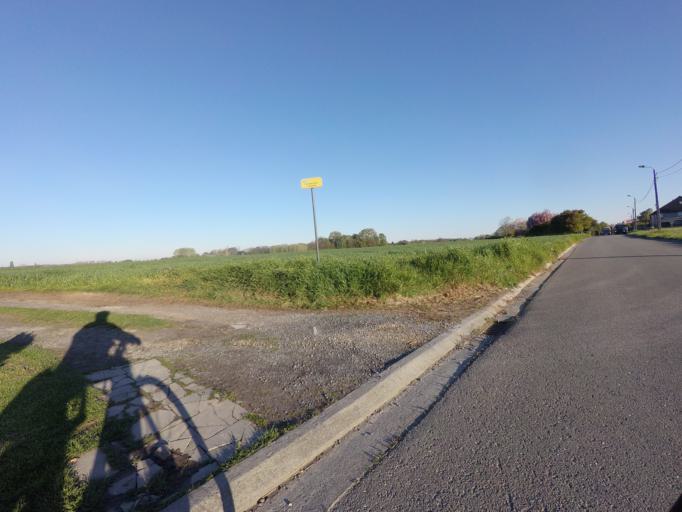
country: BE
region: Flanders
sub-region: Provincie Vlaams-Brabant
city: Zemst
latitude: 50.9742
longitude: 4.4548
